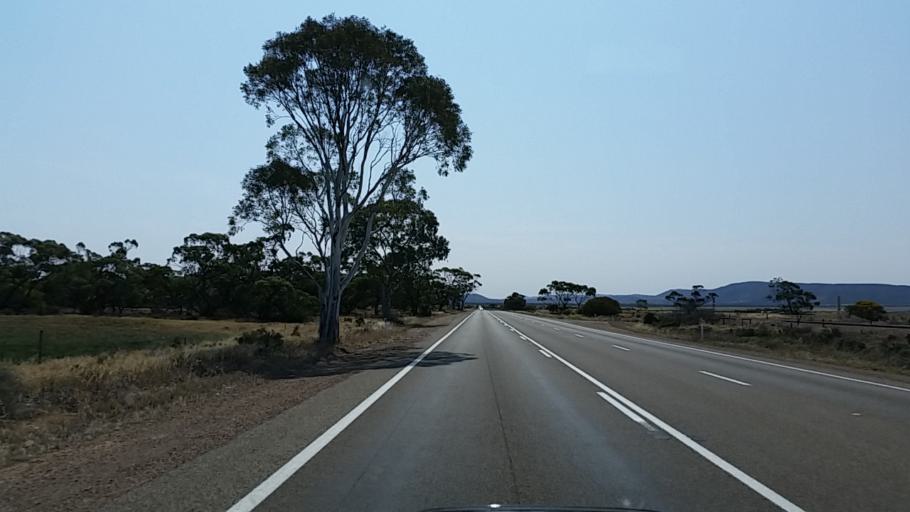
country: AU
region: South Australia
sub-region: Port Pirie City and Dists
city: Port Pirie
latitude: -32.9059
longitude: 137.9823
